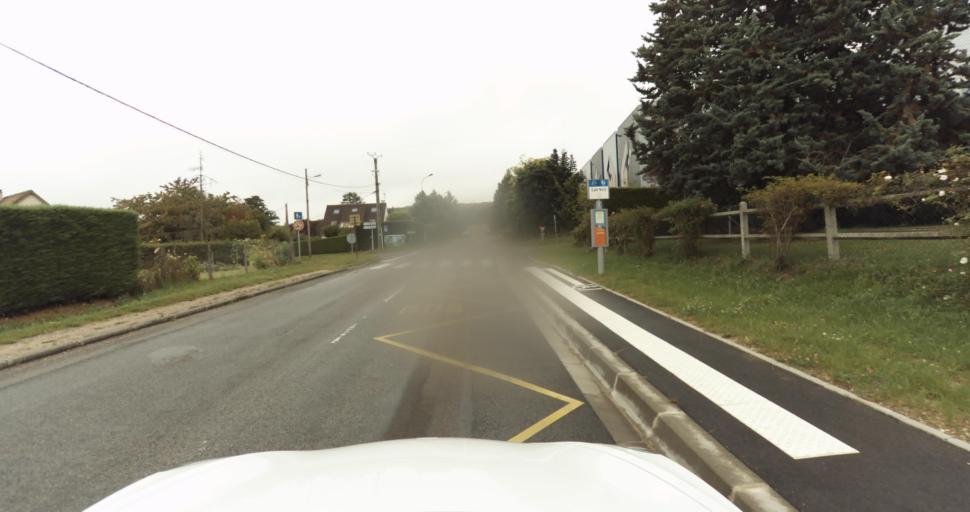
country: FR
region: Haute-Normandie
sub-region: Departement de l'Eure
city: Gravigny
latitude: 49.0688
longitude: 1.1719
